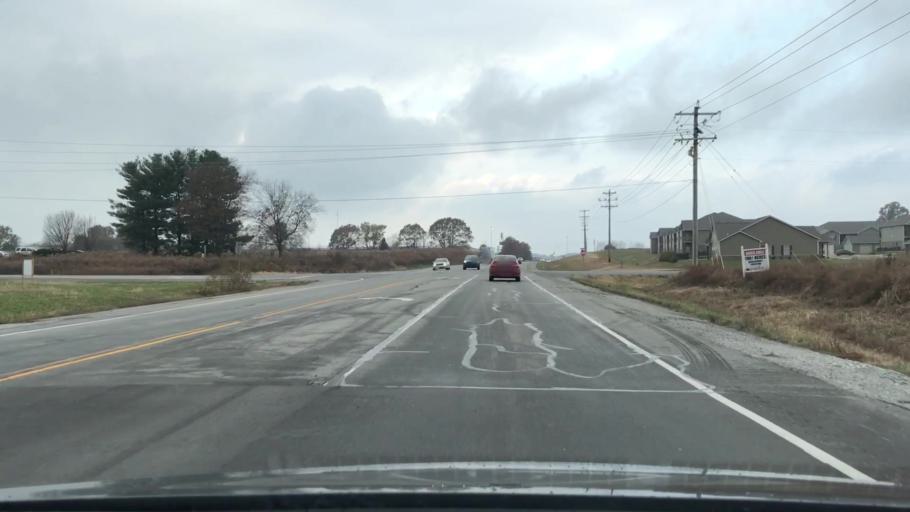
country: US
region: Kentucky
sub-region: Simpson County
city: Franklin
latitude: 36.7138
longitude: -86.5108
